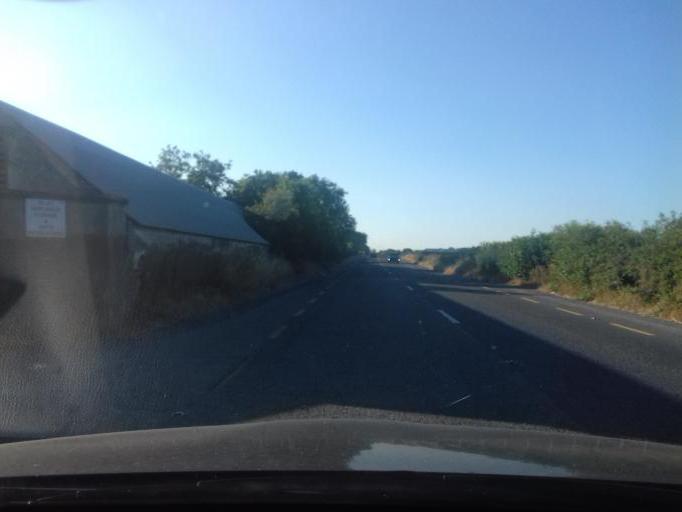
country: IE
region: Leinster
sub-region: Fingal County
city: Blanchardstown
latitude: 53.4532
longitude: -6.3467
